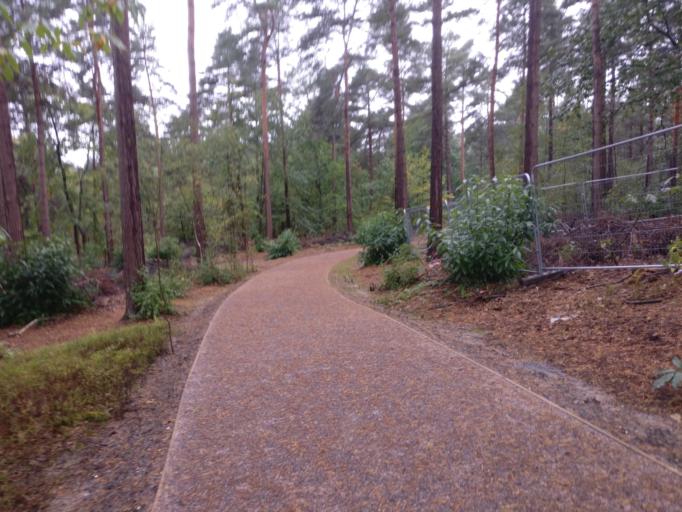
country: GB
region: England
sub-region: Surrey
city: Frimley
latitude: 51.3157
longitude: -0.7065
